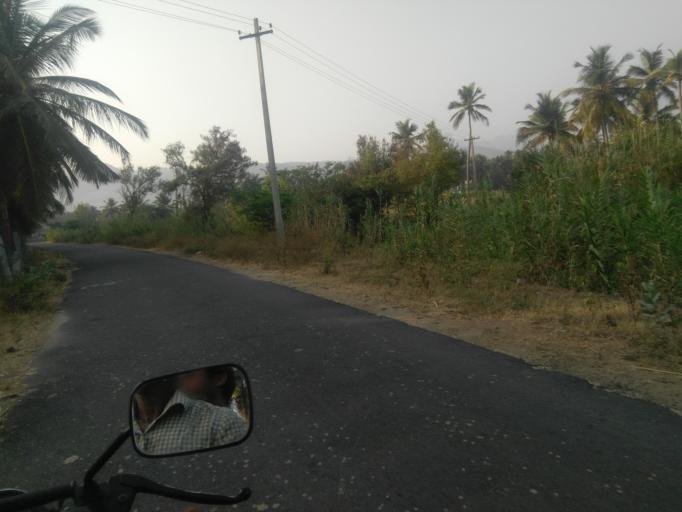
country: IN
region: Tamil Nadu
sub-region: Coimbatore
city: Karamadai
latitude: 11.2146
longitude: 76.8887
